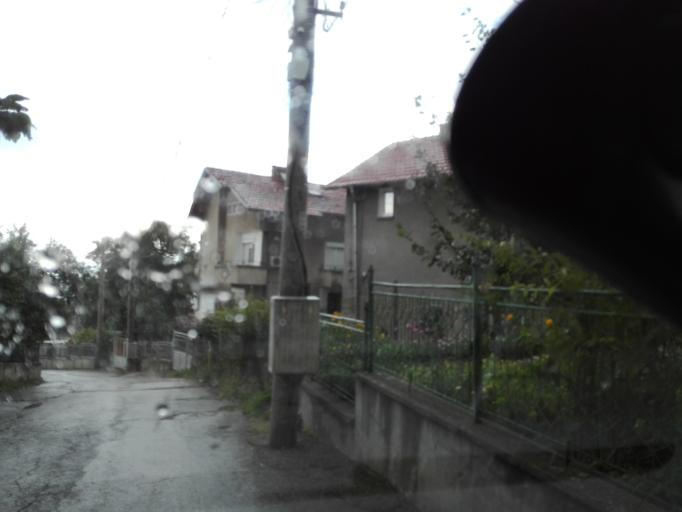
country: BG
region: Sofiya
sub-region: Obshtina Elin Pelin
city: Elin Pelin
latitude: 42.5996
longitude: 23.4837
